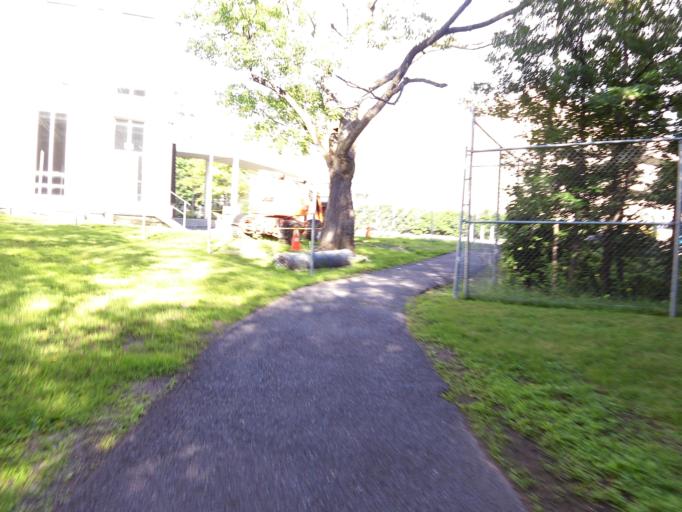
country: CA
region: Ontario
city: Bells Corners
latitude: 45.3519
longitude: -75.8532
